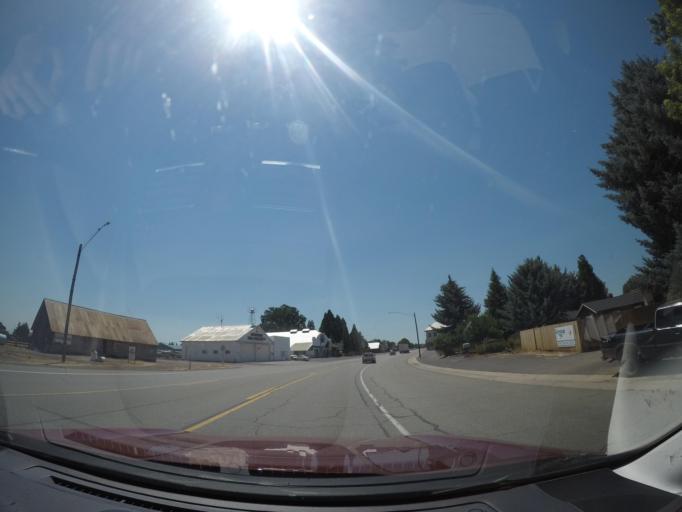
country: US
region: California
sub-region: Shasta County
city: Burney
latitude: 41.0505
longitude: -121.3961
